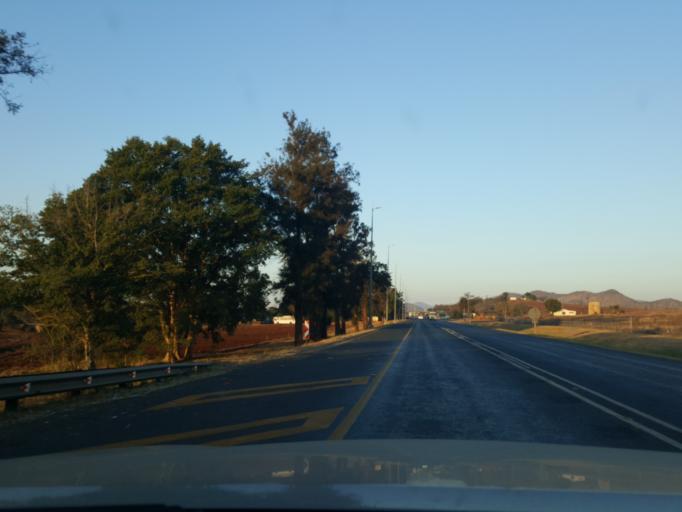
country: SZ
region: Hhohho
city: Ntfonjeni
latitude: -25.5366
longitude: 31.3368
